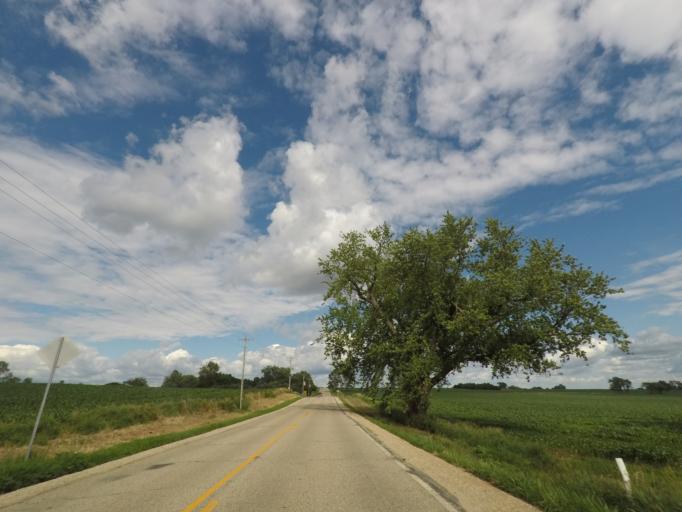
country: US
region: Wisconsin
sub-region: Rock County
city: Orfordville
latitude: 42.7139
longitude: -89.2229
